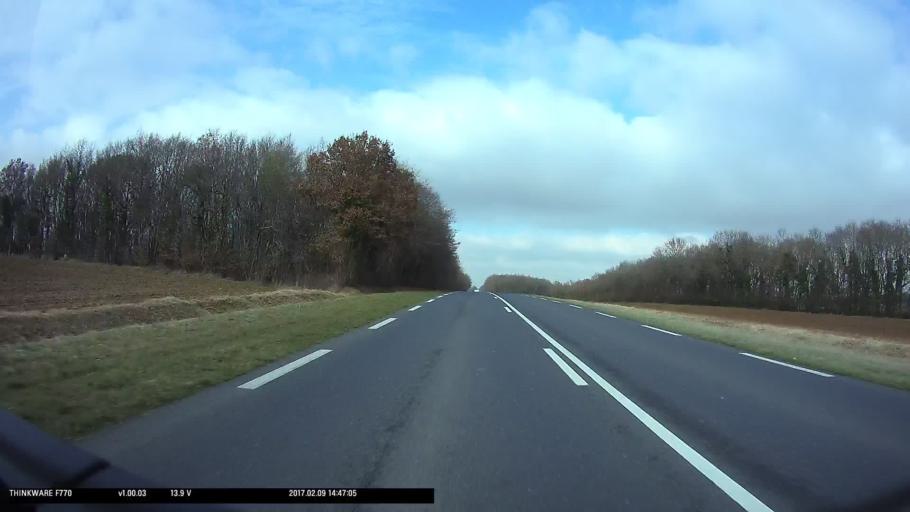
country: FR
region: Centre
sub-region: Departement du Cher
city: Trouy
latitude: 46.9789
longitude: 2.3965
